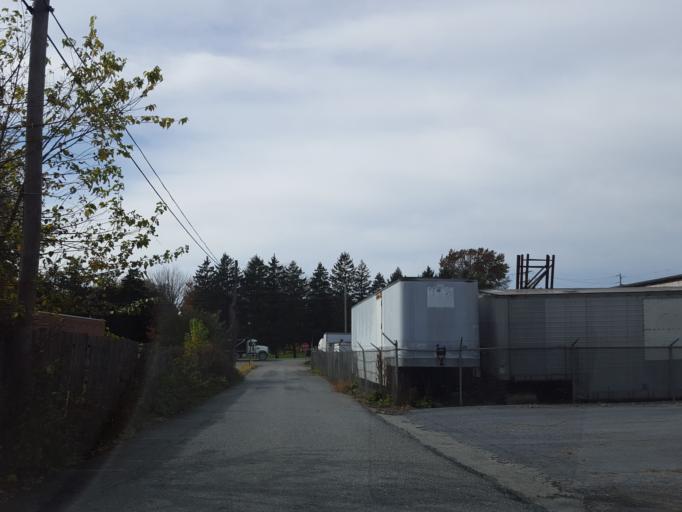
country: US
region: Pennsylvania
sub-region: York County
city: Wrightsville
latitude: 40.0228
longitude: -76.5406
